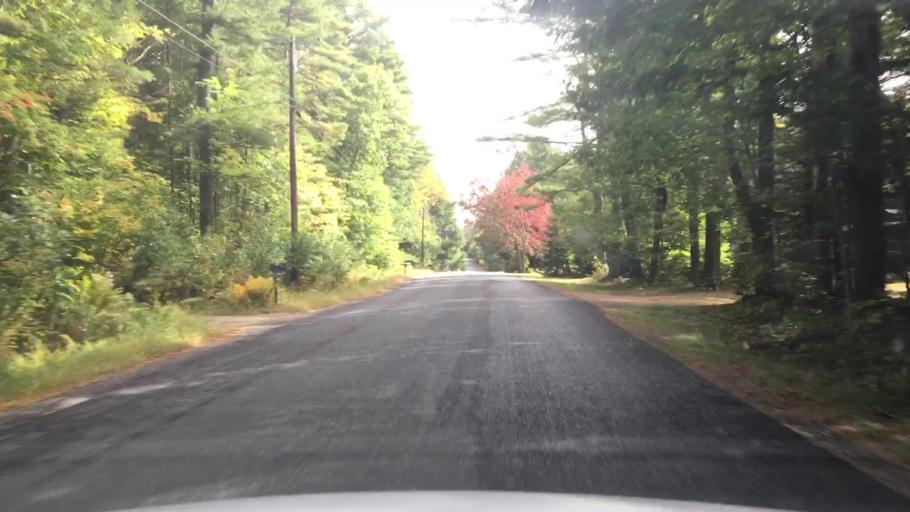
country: US
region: Maine
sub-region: Androscoggin County
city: Lisbon Falls
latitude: 43.9795
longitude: -70.0940
